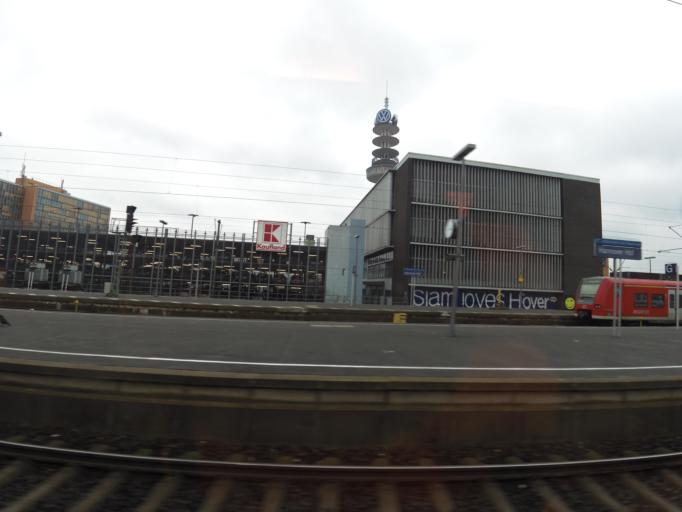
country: DE
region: Lower Saxony
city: Hannover
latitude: 52.3787
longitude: 9.7389
